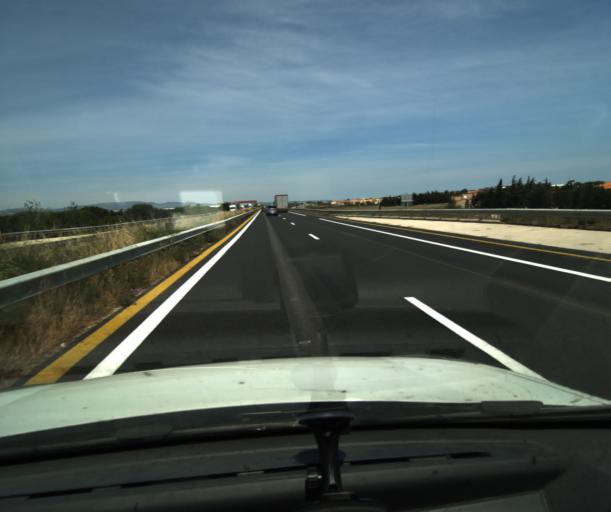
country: FR
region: Languedoc-Roussillon
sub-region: Departement des Pyrenees-Orientales
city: Saint-Esteve
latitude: 42.7165
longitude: 2.8725
